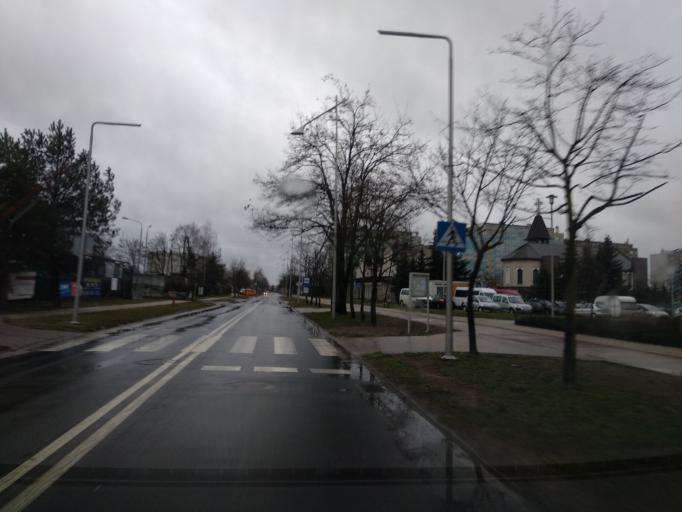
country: PL
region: Lower Silesian Voivodeship
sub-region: Powiat polkowicki
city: Polkowice
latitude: 51.5095
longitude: 16.0798
